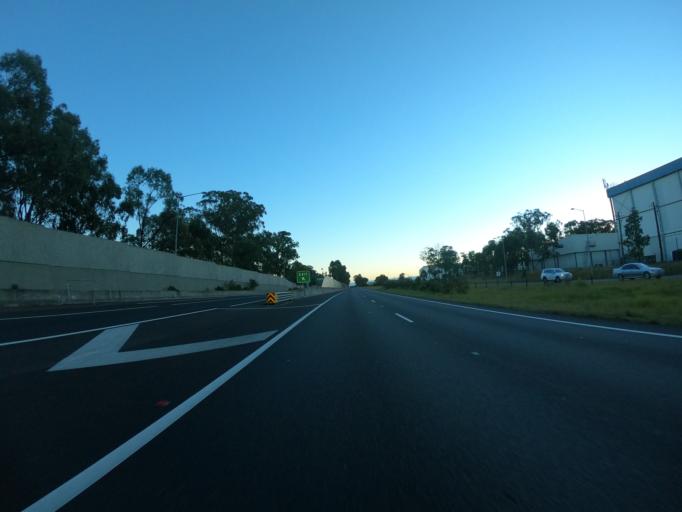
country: AU
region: New South Wales
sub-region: Blacktown
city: Glendenning
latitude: -33.7645
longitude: 150.8460
